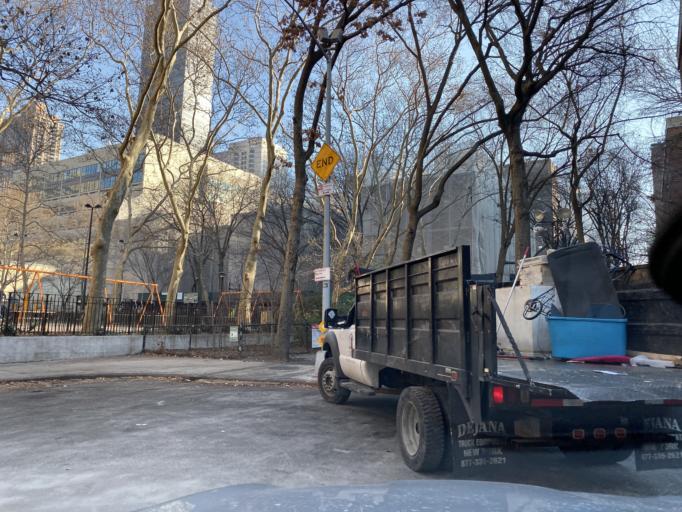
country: US
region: New York
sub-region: New York County
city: Manhattan
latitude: 40.7735
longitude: -73.9873
